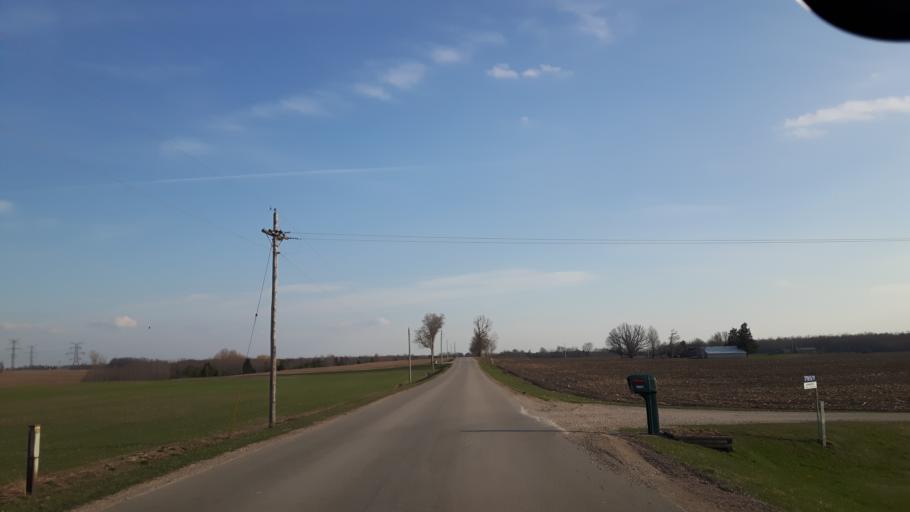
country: CA
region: Ontario
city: Goderich
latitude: 43.6931
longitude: -81.6645
